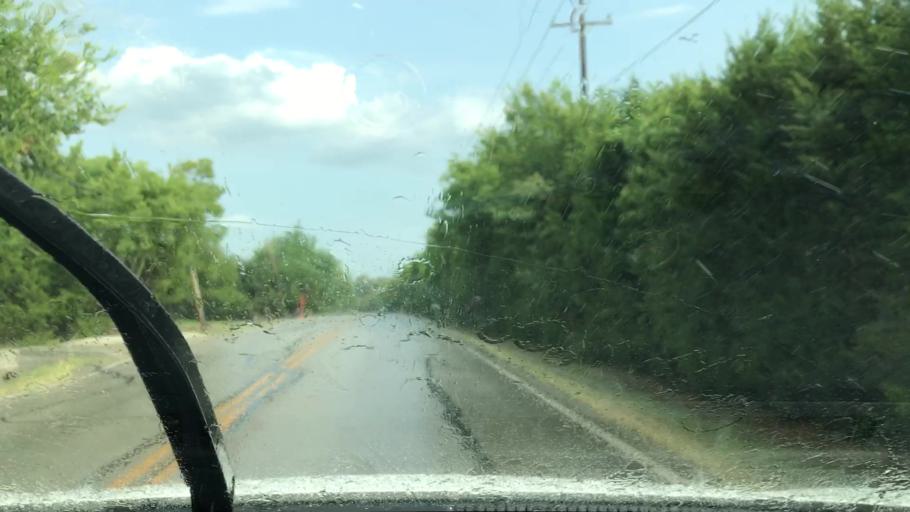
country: US
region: Texas
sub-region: Collin County
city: Wylie
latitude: 32.9542
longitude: -96.5241
